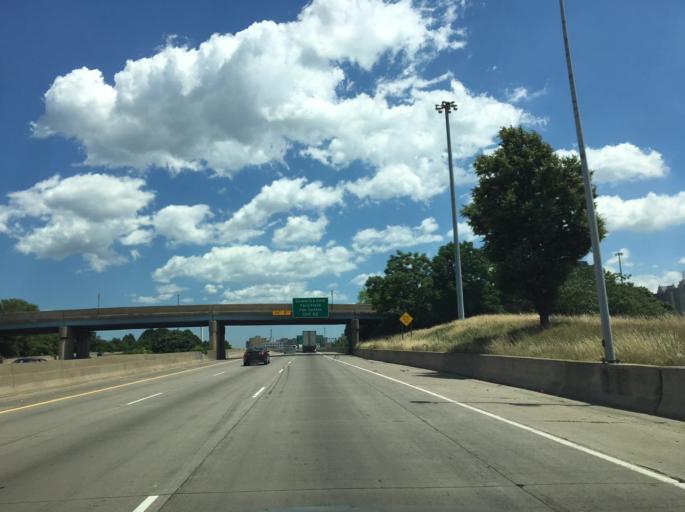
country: US
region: Michigan
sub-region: Wayne County
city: Detroit
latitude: 42.3348
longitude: -83.0668
